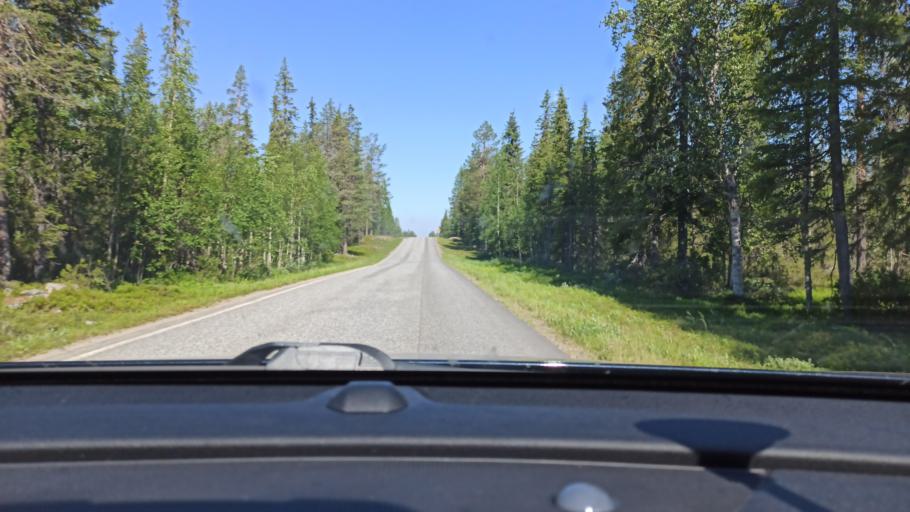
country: FI
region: Lapland
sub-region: Tunturi-Lappi
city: Kolari
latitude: 67.6742
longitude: 24.1457
